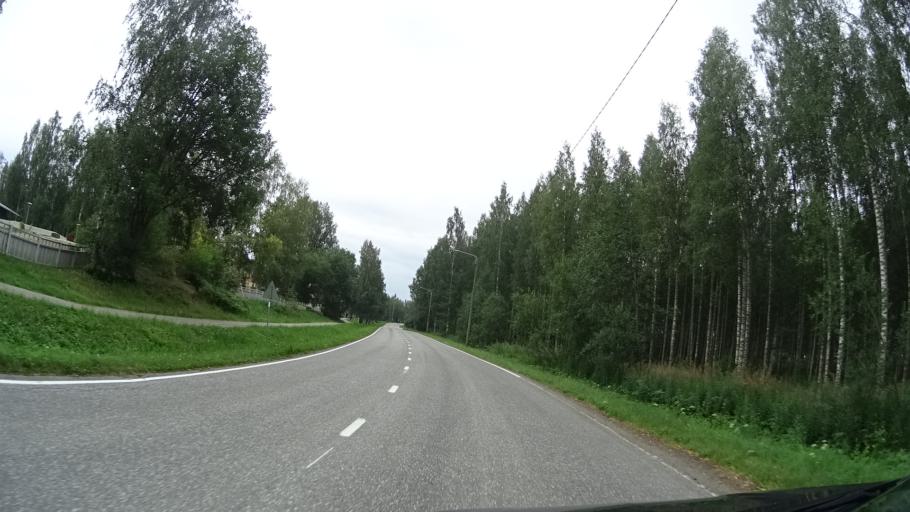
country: FI
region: Southern Savonia
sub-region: Savonlinna
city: Punkaharju
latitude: 61.7544
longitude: 29.3863
